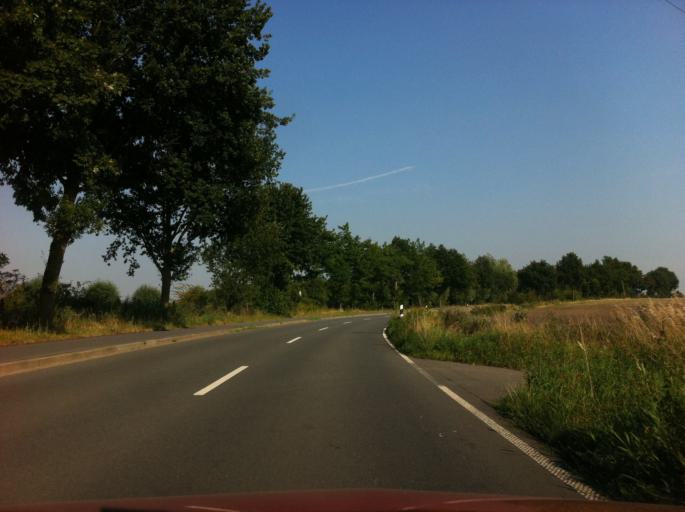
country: DE
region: Schleswig-Holstein
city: Harmsdorf
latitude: 54.3110
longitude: 10.8166
